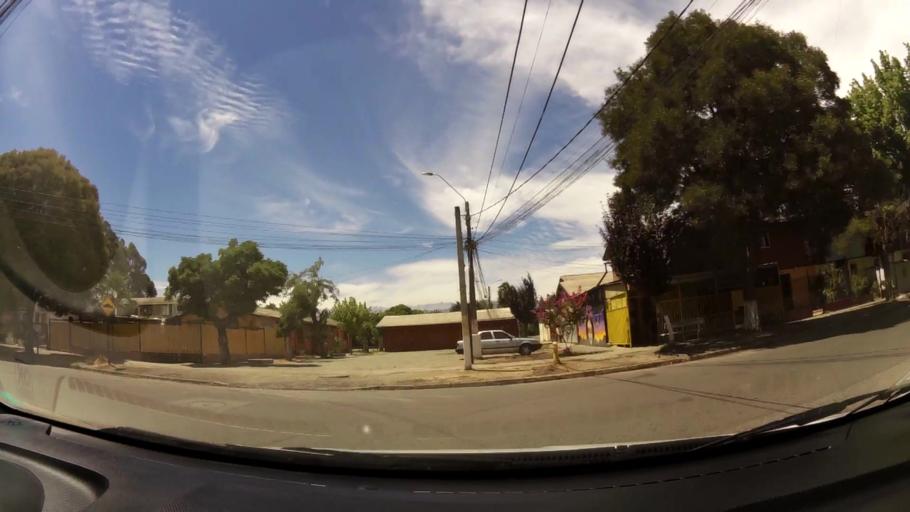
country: CL
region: O'Higgins
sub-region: Provincia de Cachapoal
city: Graneros
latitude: -34.0607
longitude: -70.7261
